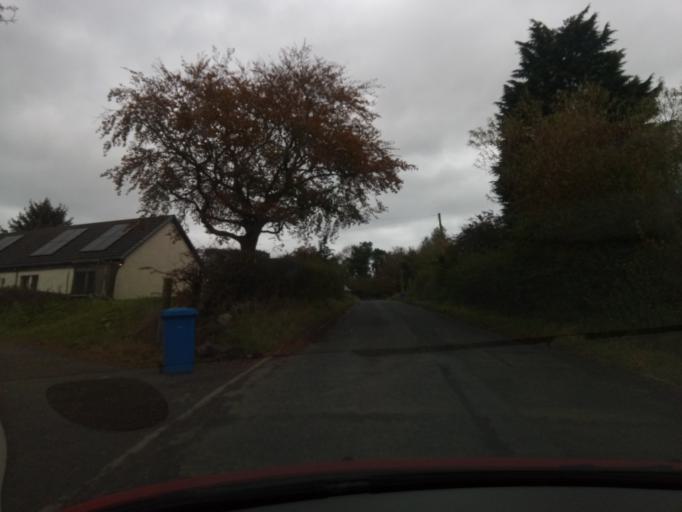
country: GB
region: Scotland
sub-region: West Lothian
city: Bathgate
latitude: 55.9167
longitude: -3.6380
